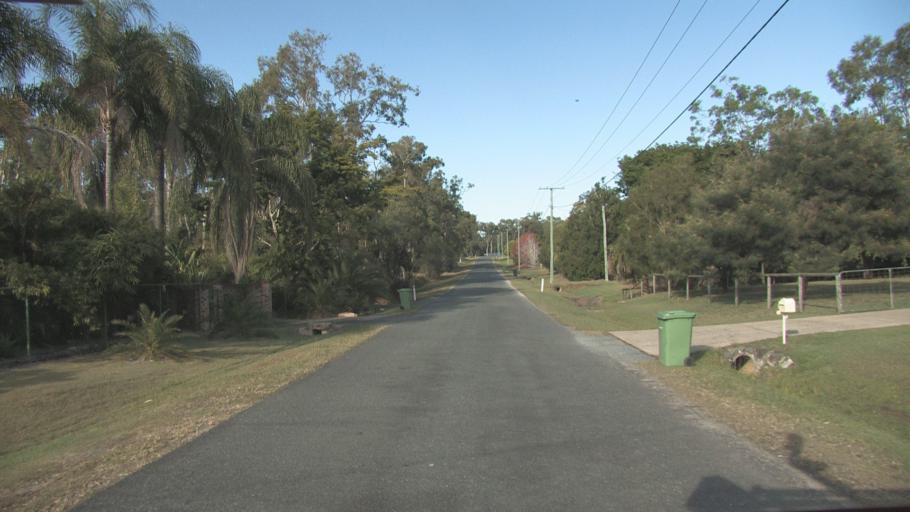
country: AU
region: Queensland
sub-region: Logan
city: Park Ridge South
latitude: -27.7436
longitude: 153.0294
